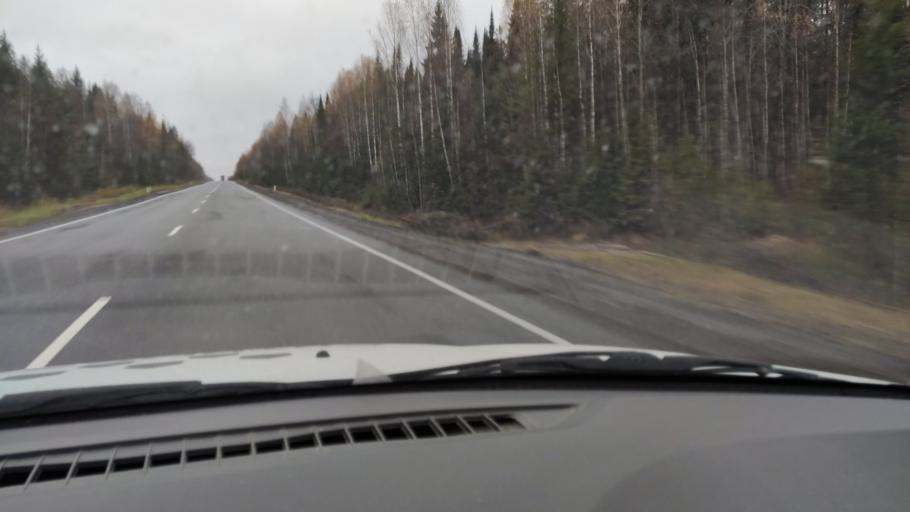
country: RU
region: Kirov
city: Omutninsk
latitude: 58.7598
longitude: 52.0150
